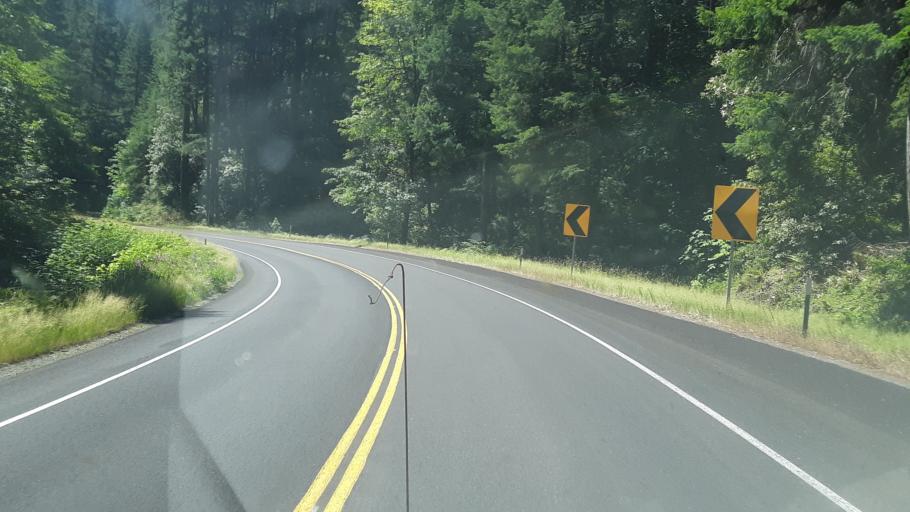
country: US
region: Oregon
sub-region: Josephine County
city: Cave Junction
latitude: 41.9340
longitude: -123.7570
